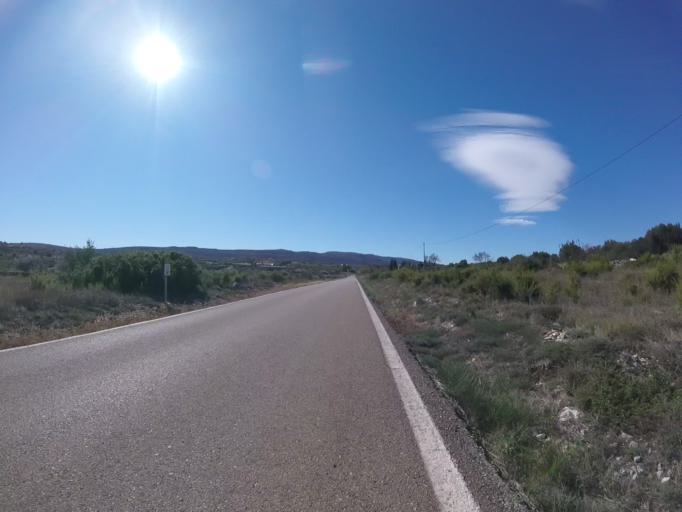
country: ES
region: Valencia
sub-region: Provincia de Castello
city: Albocasser
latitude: 40.3732
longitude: 0.0198
